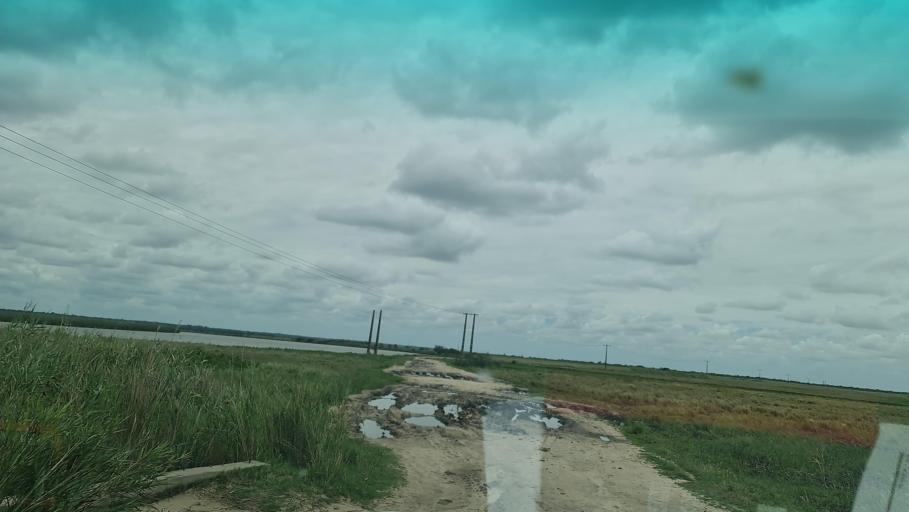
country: MZ
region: Maputo City
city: Maputo
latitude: -25.7232
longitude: 32.6995
